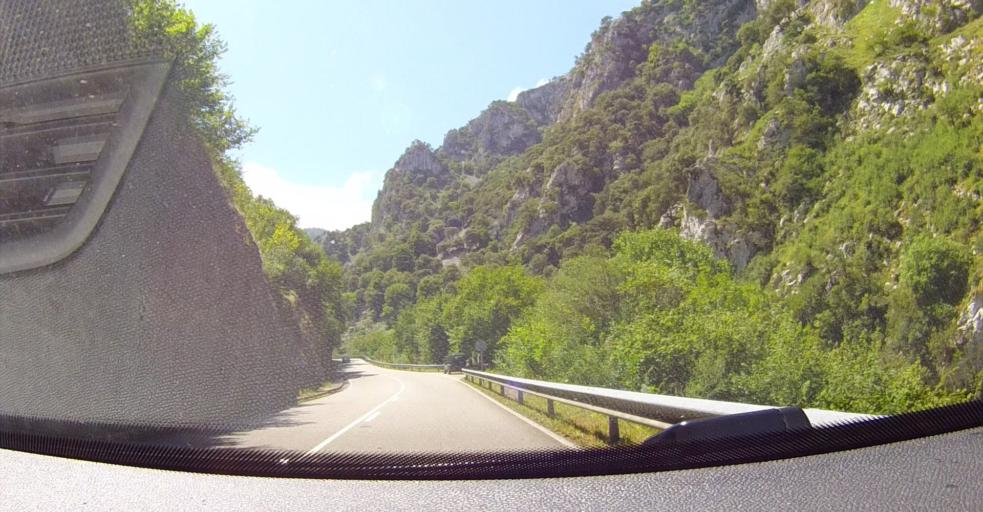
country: ES
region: Cantabria
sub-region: Provincia de Cantabria
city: Tresviso
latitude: 43.3046
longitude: -4.7438
